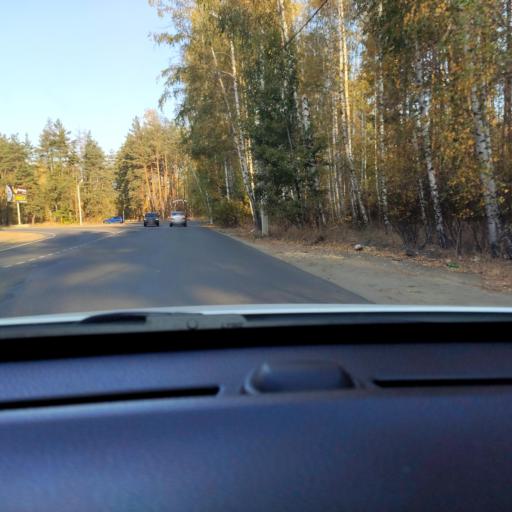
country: RU
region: Voronezj
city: Somovo
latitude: 51.6952
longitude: 39.3138
